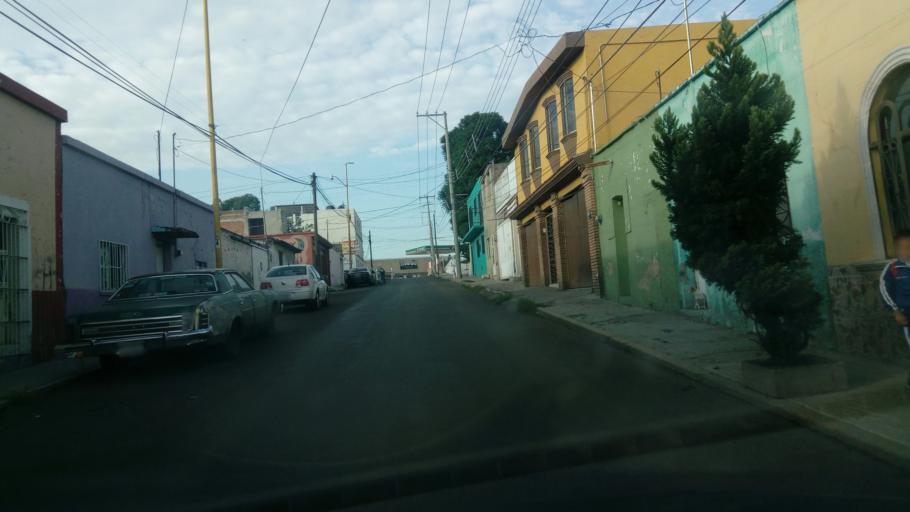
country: MX
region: Durango
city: Victoria de Durango
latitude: 24.0167
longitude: -104.6763
